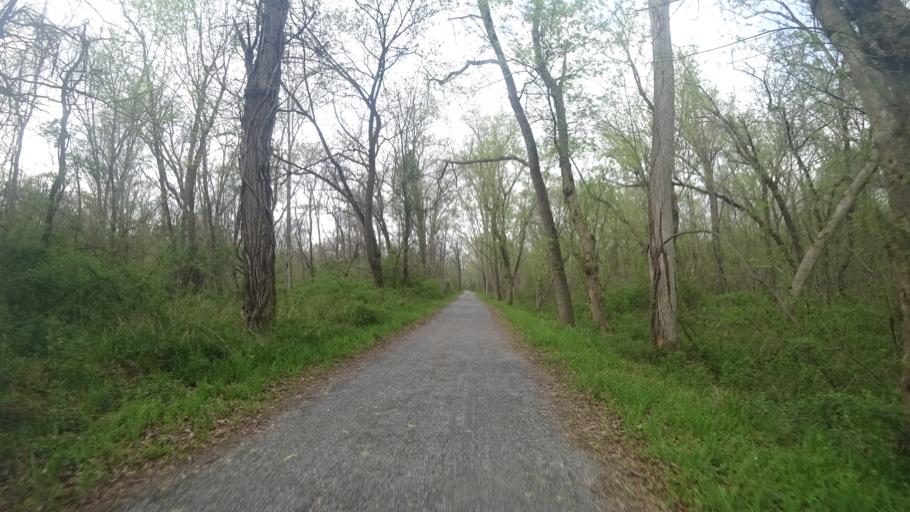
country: US
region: Virginia
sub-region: Loudoun County
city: Belmont
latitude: 39.1079
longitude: -77.4746
